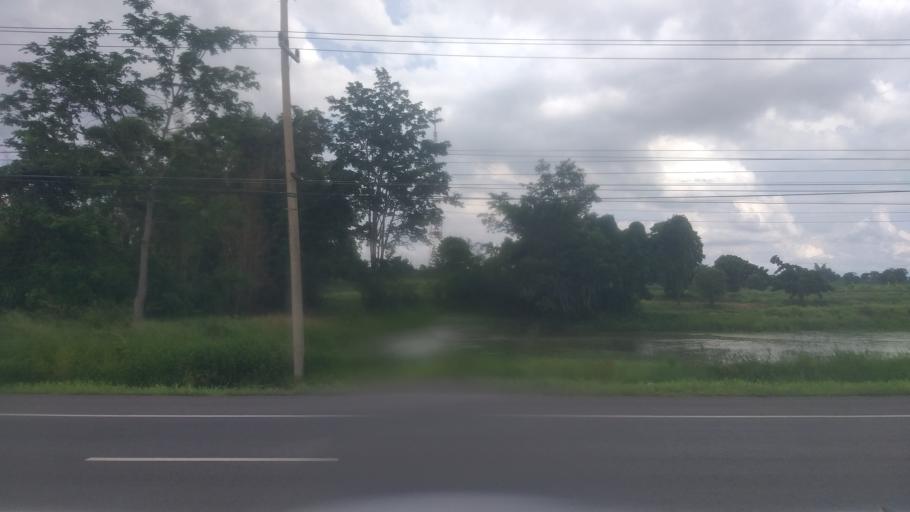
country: TH
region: Chaiyaphum
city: Noen Sa-nga
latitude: 15.6694
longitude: 101.9591
